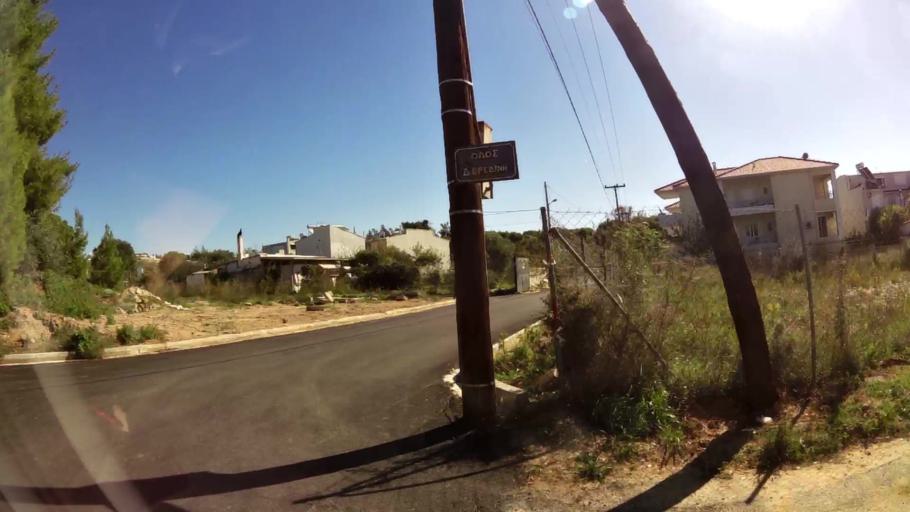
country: GR
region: Attica
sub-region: Nomarchia Athinas
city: Nea Erythraia
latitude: 38.0936
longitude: 23.7898
